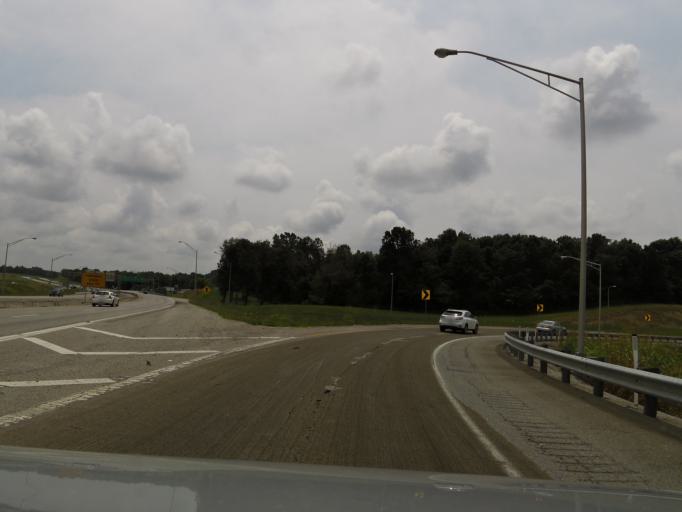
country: US
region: Kentucky
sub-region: Hardin County
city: Elizabethtown
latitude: 37.6722
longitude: -85.8497
